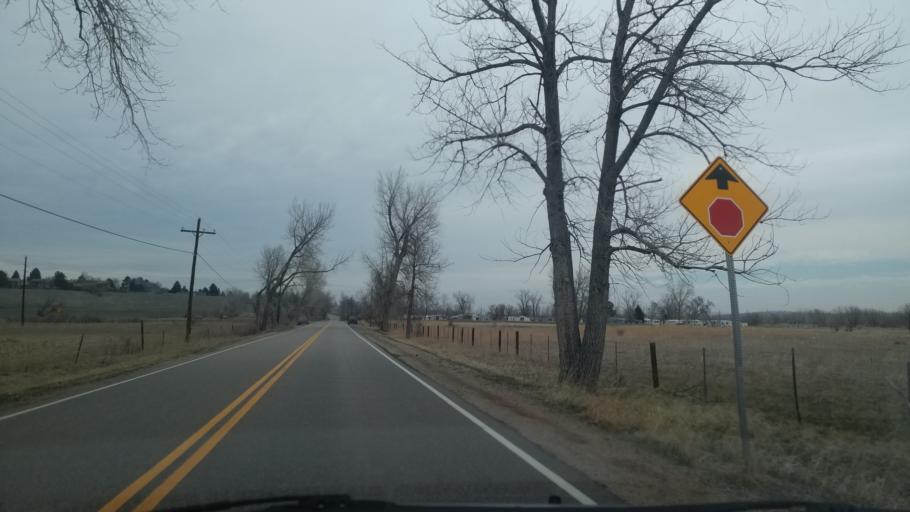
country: US
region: Colorado
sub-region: Boulder County
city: Boulder
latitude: 39.9664
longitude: -105.2366
